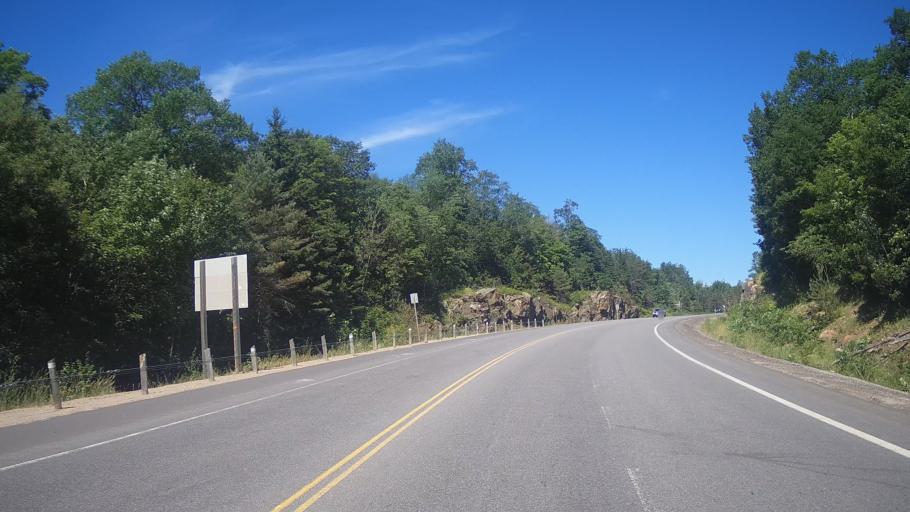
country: CA
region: Ontario
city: Huntsville
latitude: 45.3367
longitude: -79.2087
